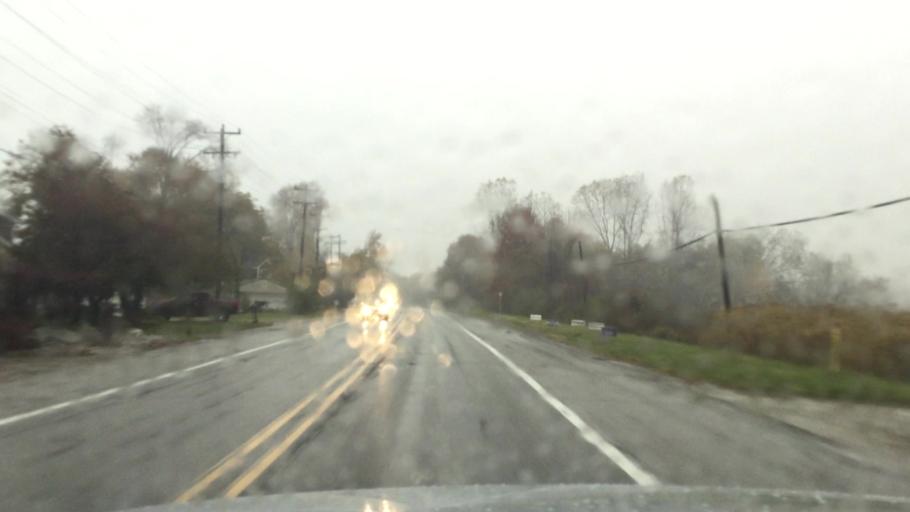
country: US
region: Michigan
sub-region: Macomb County
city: New Baltimore
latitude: 42.6879
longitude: -82.6749
